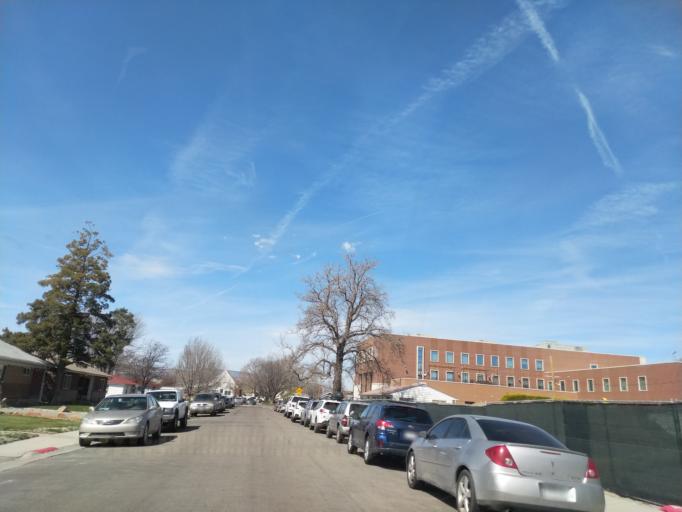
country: US
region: Colorado
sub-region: Mesa County
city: Grand Junction
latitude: 39.0802
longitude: -108.5588
